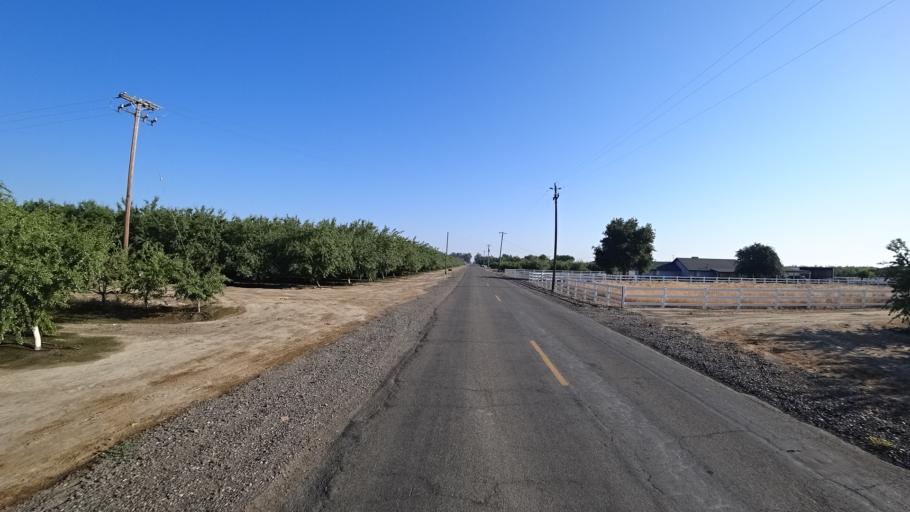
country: US
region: California
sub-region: Kings County
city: Lemoore
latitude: 36.2916
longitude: -119.7447
